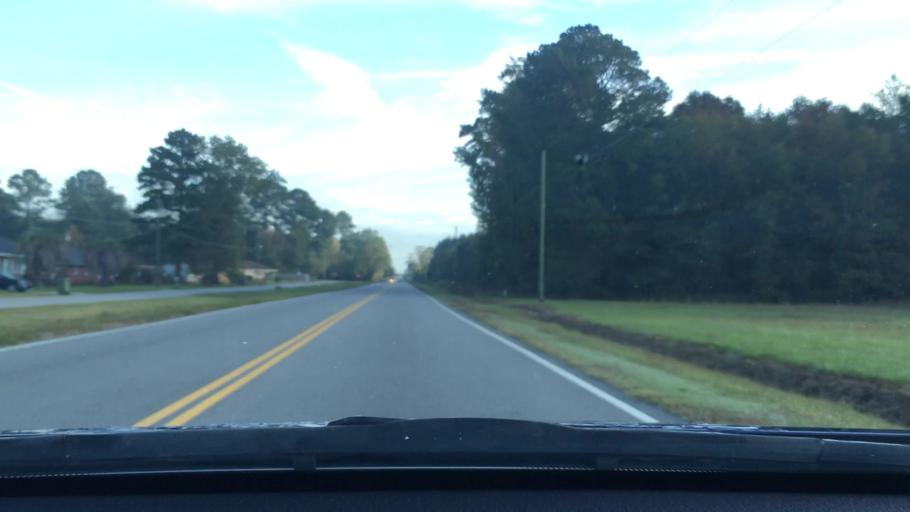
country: US
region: South Carolina
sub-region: Sumter County
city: Sumter
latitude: 33.9309
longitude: -80.3238
